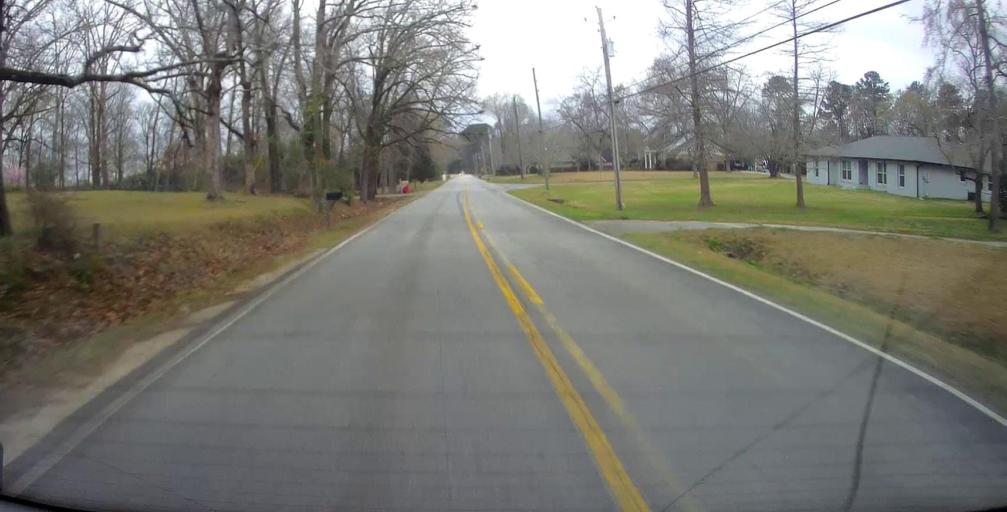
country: US
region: Georgia
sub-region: Bibb County
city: Macon
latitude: 32.8921
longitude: -83.7303
